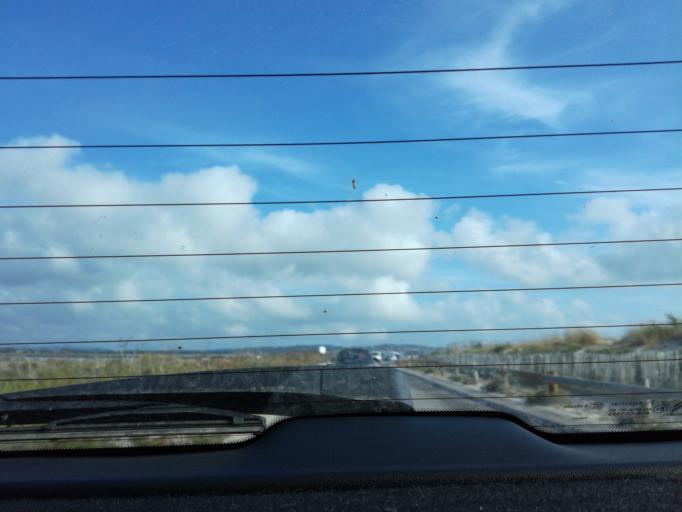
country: FR
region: Provence-Alpes-Cote d'Azur
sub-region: Departement du Var
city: Hyeres
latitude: 43.0695
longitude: 6.1298
